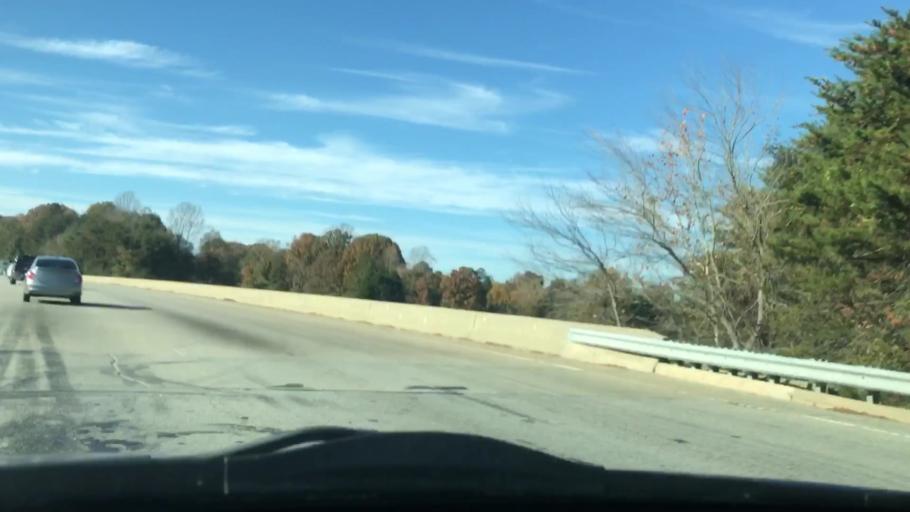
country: US
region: North Carolina
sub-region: Guilford County
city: High Point
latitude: 36.0047
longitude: -79.9953
